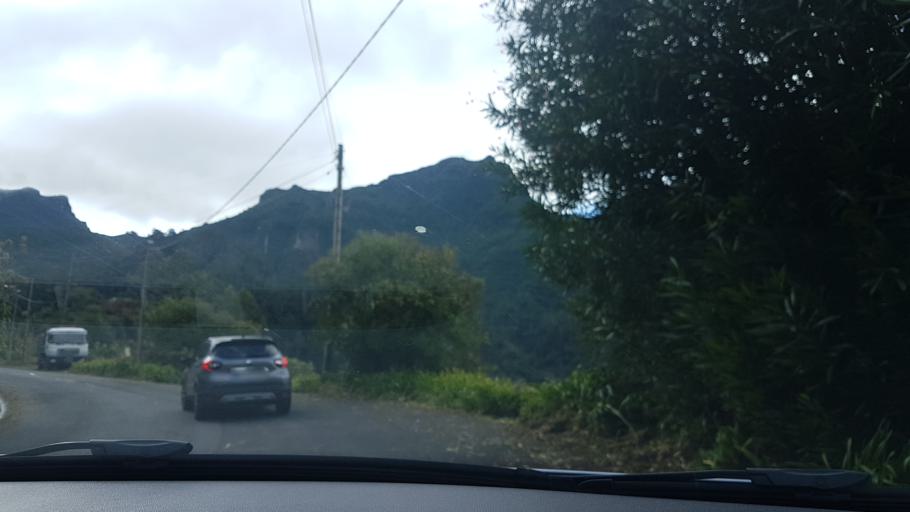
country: PT
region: Madeira
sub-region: Sao Vicente
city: Sao Vicente
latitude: 32.7769
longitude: -17.0282
